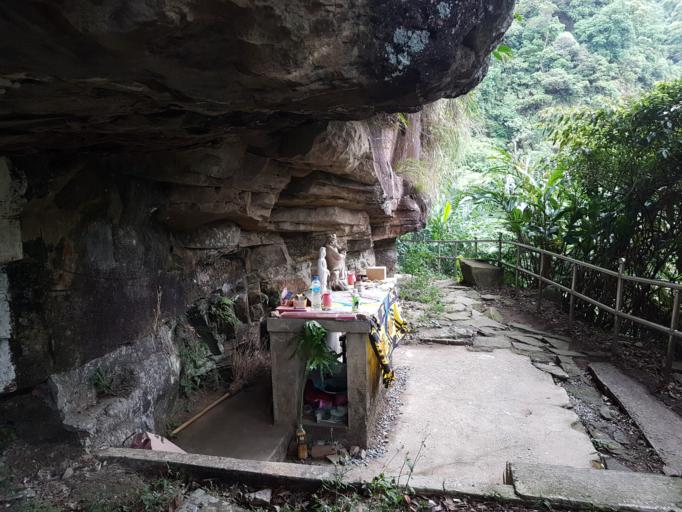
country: TW
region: Taiwan
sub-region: Keelung
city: Keelung
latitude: 25.0488
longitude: 121.6656
